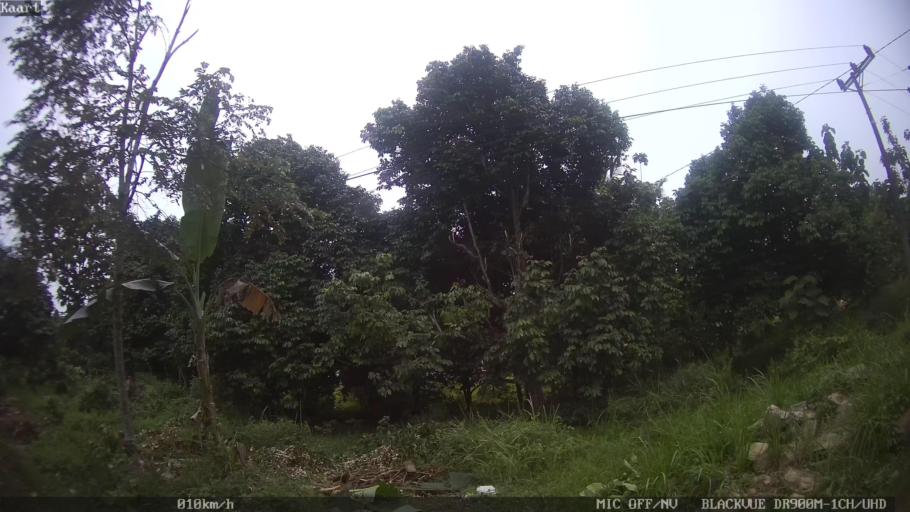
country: ID
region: Lampung
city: Panjang
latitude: -5.4215
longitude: 105.3552
